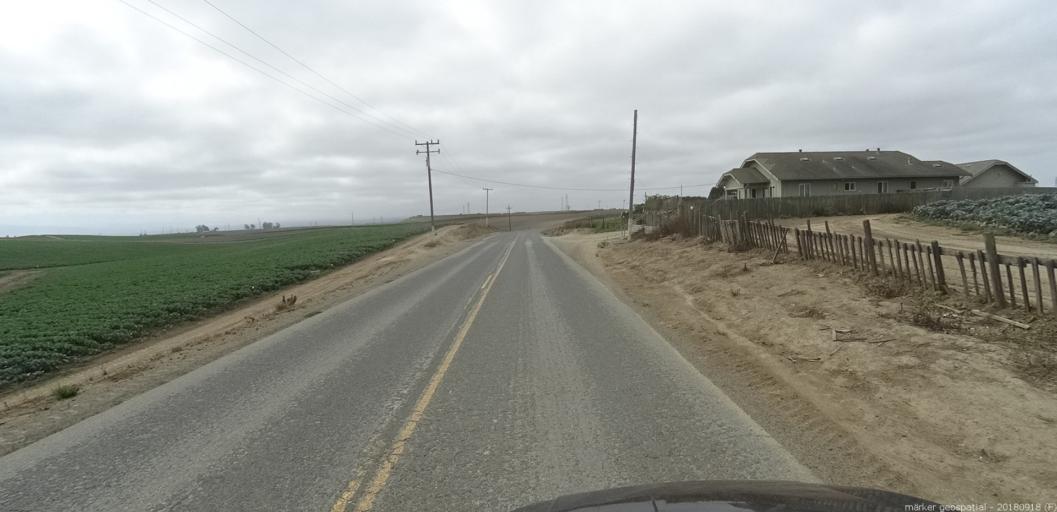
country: US
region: California
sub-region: Monterey County
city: Castroville
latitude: 36.7675
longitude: -121.7243
